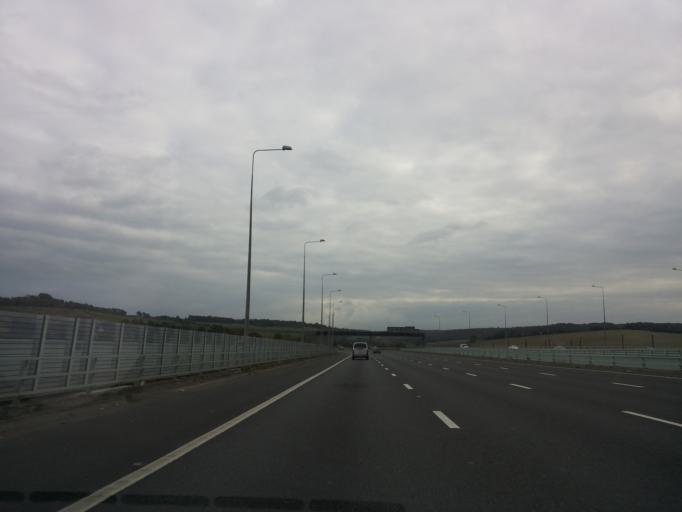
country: GB
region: England
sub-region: Medway
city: Cuxton
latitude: 51.3747
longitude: 0.4771
